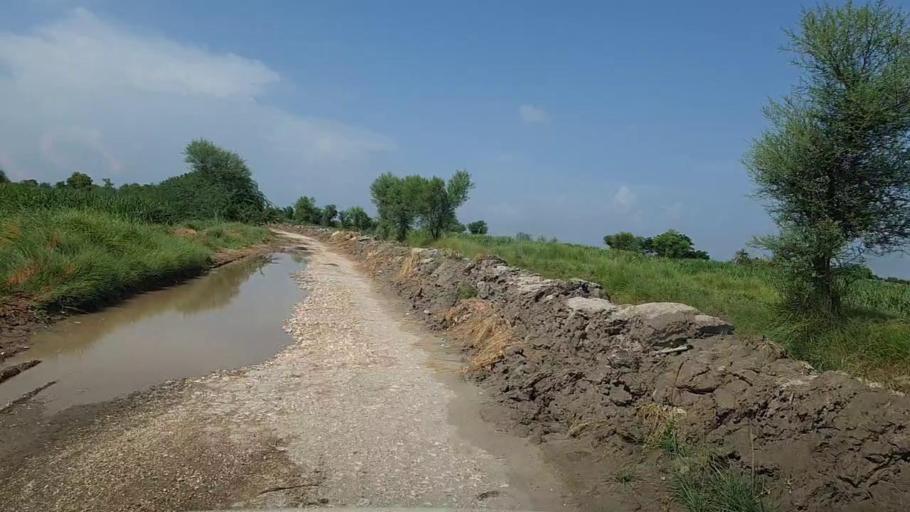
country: PK
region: Sindh
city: Bhiria
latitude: 26.8857
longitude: 68.2365
